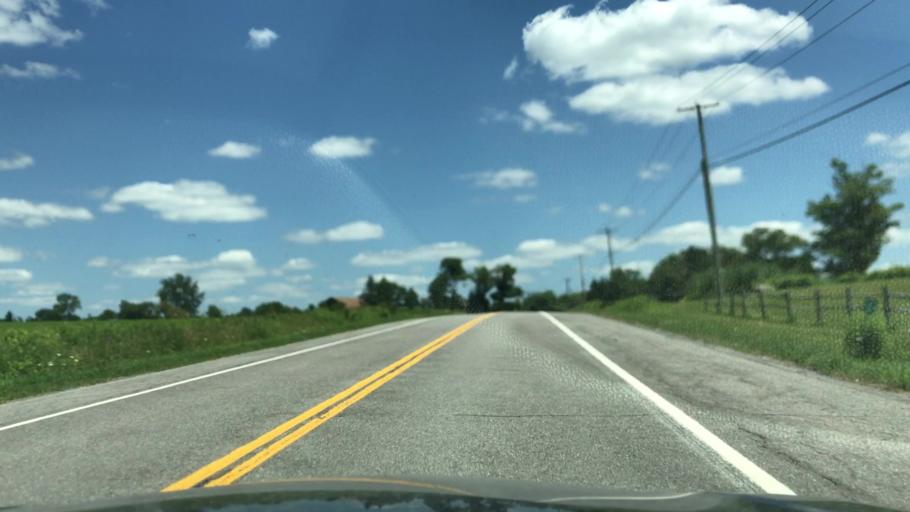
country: US
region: New York
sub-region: Erie County
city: Alden
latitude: 42.7704
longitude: -78.4712
